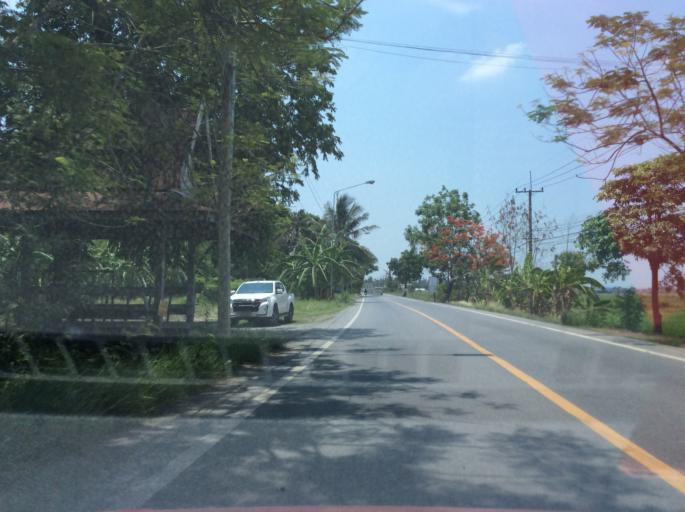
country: TH
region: Pathum Thani
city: Ban Lam Luk Ka
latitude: 14.0045
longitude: 100.7792
